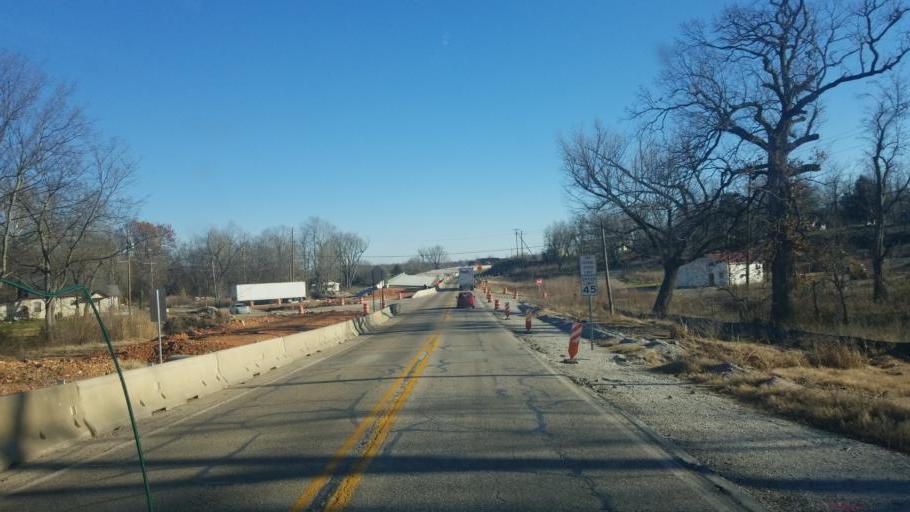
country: US
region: Arkansas
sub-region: Boone County
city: Harrison
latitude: 36.1569
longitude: -92.9940
